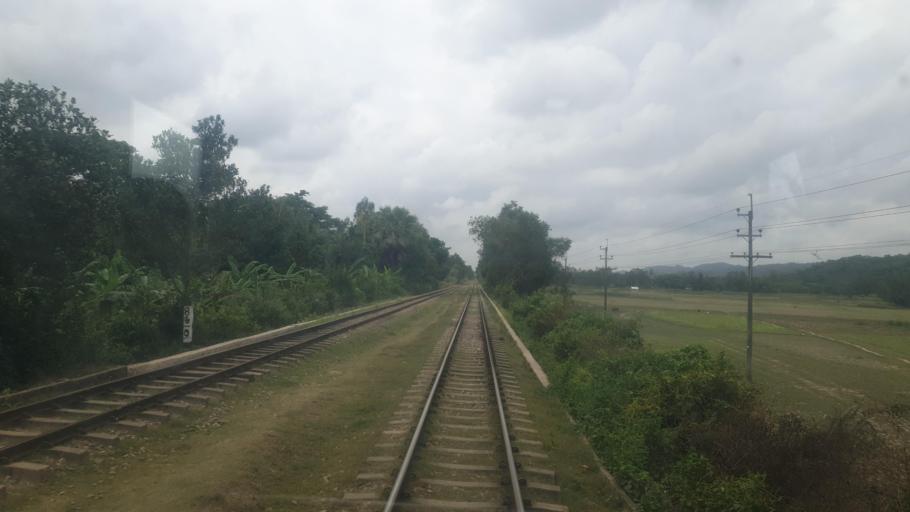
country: BD
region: Chittagong
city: Fatikchari
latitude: 22.6965
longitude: 91.6254
